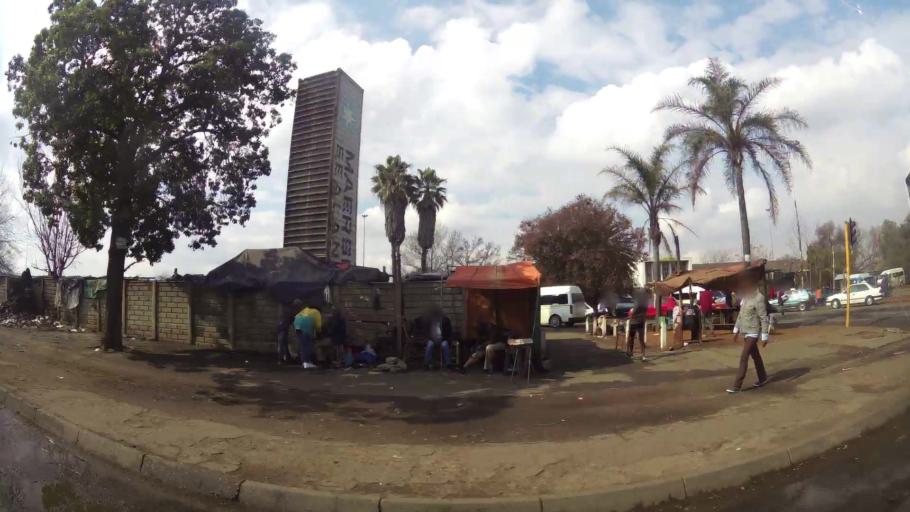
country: ZA
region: Gauteng
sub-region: Sedibeng District Municipality
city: Vereeniging
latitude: -26.6739
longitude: 27.9340
